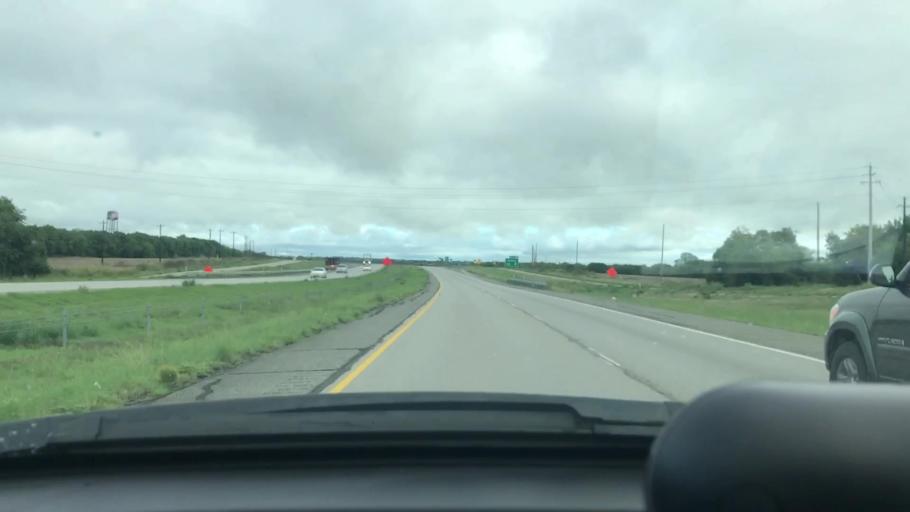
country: US
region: Texas
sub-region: Collin County
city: Anna
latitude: 33.3755
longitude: -96.5810
